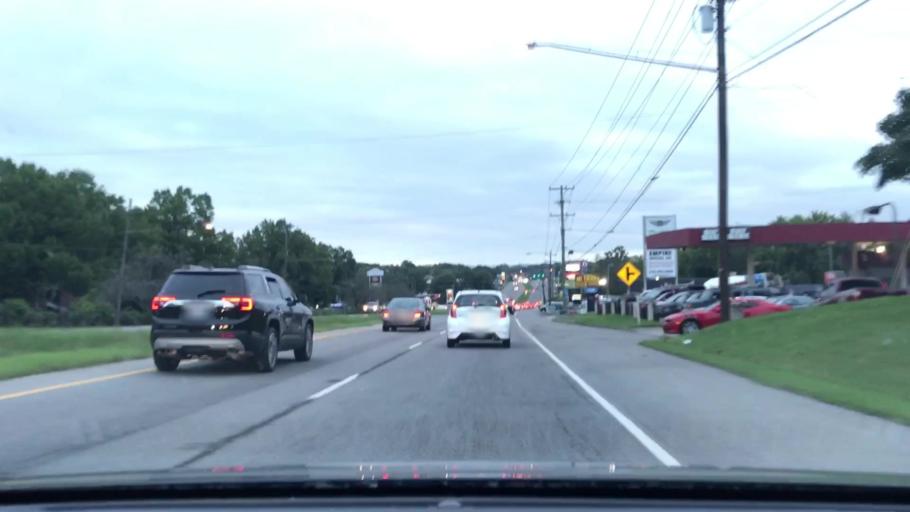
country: US
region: Tennessee
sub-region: Williamson County
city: Brentwood Estates
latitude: 36.0552
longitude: -86.7154
